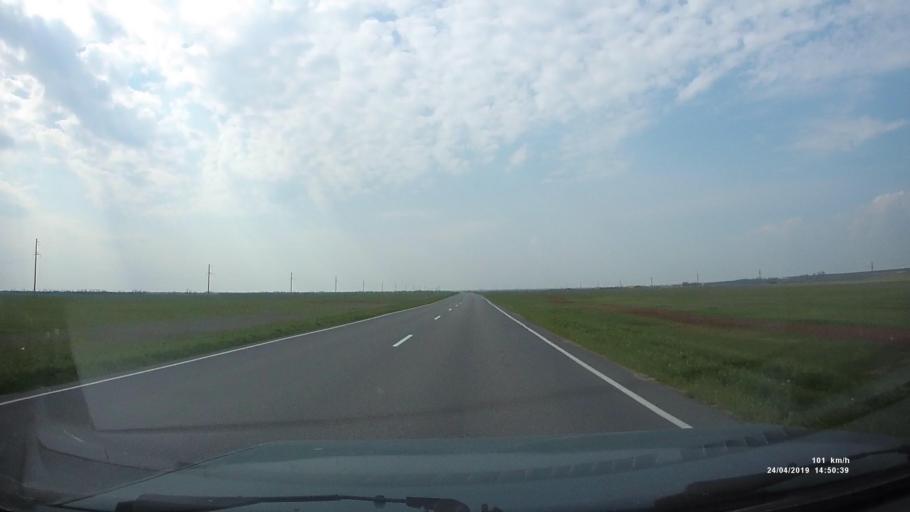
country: RU
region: Rostov
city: Remontnoye
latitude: 46.5189
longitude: 43.7155
